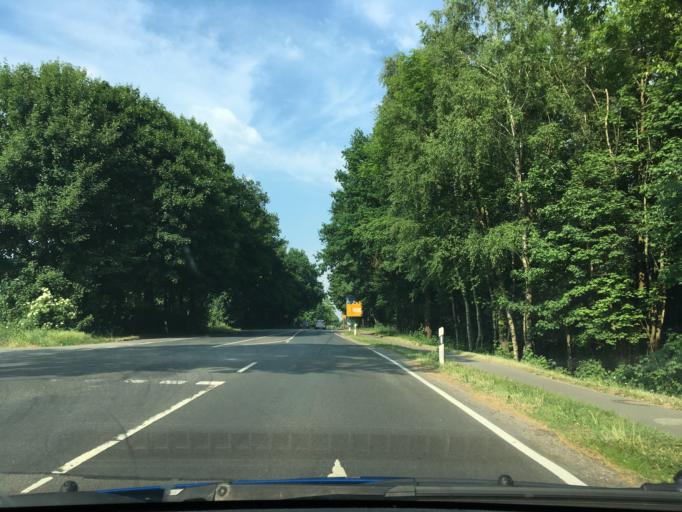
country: DE
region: Lower Saxony
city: Buchholz in der Nordheide
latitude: 53.3736
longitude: 9.8863
